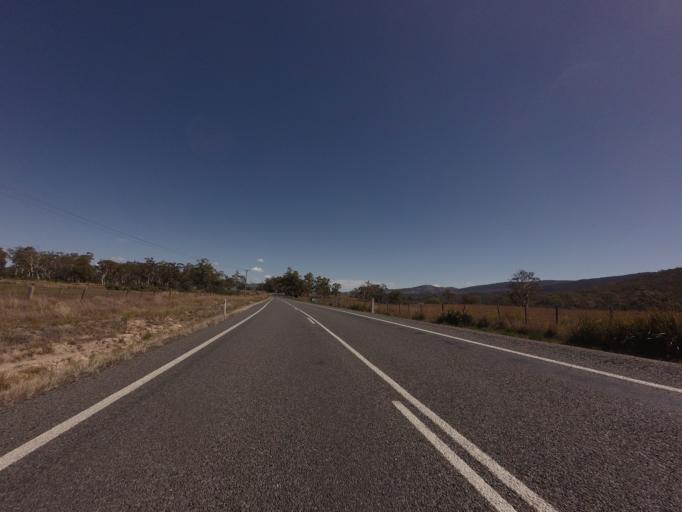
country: AU
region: Tasmania
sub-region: Northern Midlands
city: Evandale
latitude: -41.7541
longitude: 147.7593
